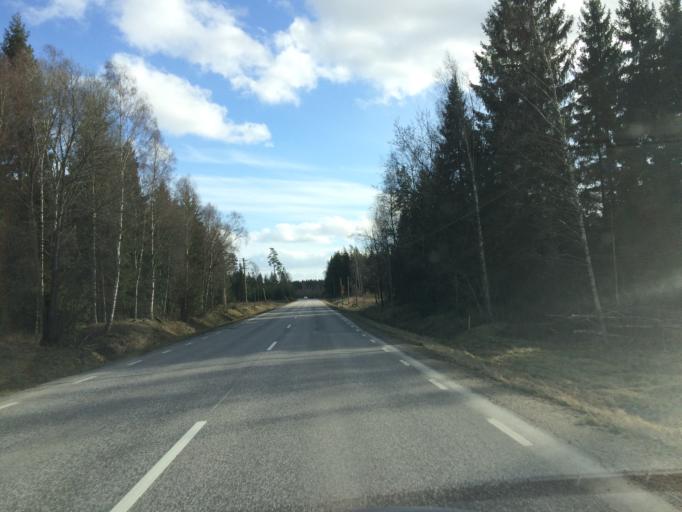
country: SE
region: Kronoberg
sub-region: Almhults Kommun
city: AElmhult
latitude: 56.5857
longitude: 14.0985
